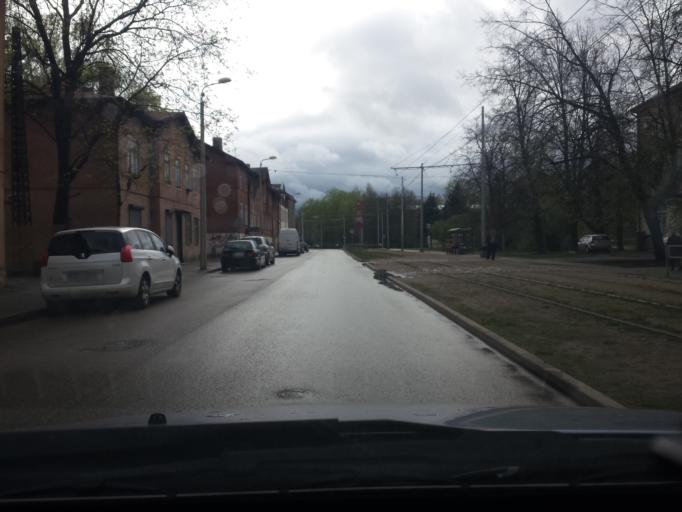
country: LV
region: Riga
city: Jaunciems
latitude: 56.9795
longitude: 24.1775
